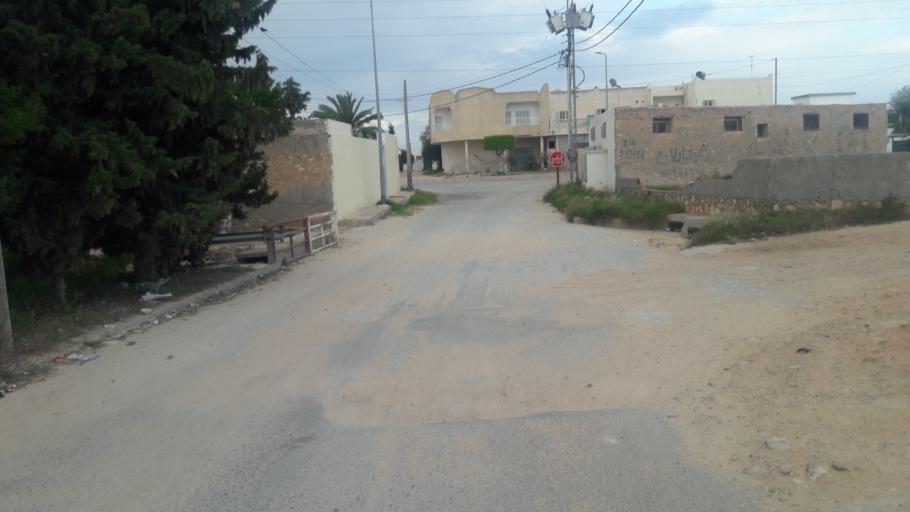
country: TN
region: Safaqis
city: Al Qarmadah
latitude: 34.8102
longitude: 10.7486
